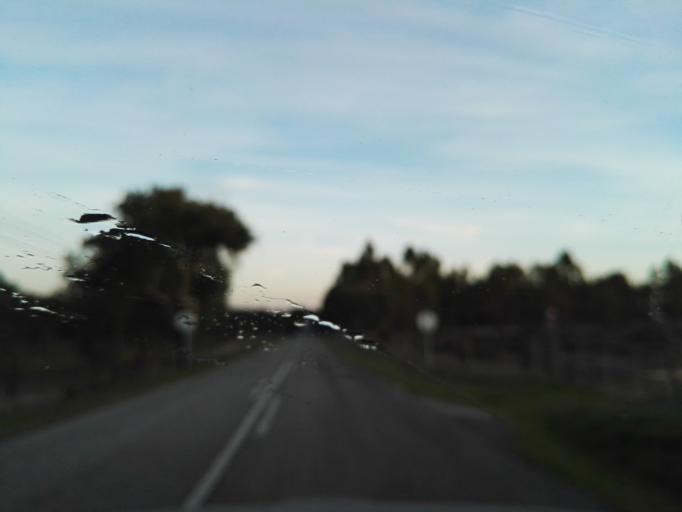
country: PT
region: Evora
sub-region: Montemor-O-Novo
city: Montemor-o-Novo
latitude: 38.7819
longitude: -8.2179
